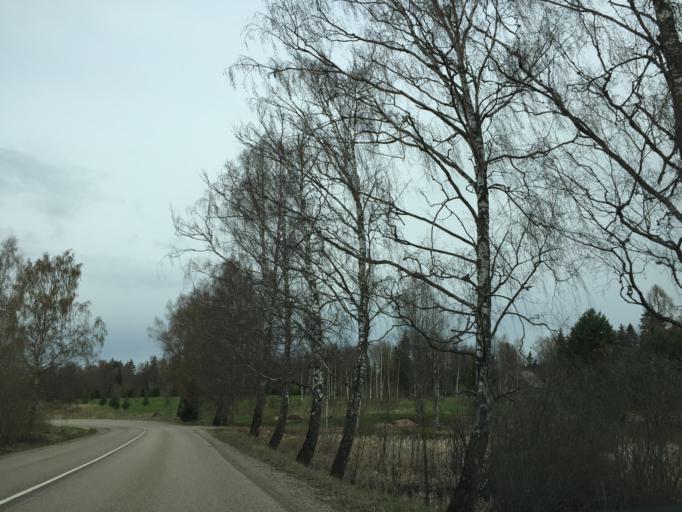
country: LV
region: Amatas Novads
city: Drabesi
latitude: 57.2576
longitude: 25.2757
